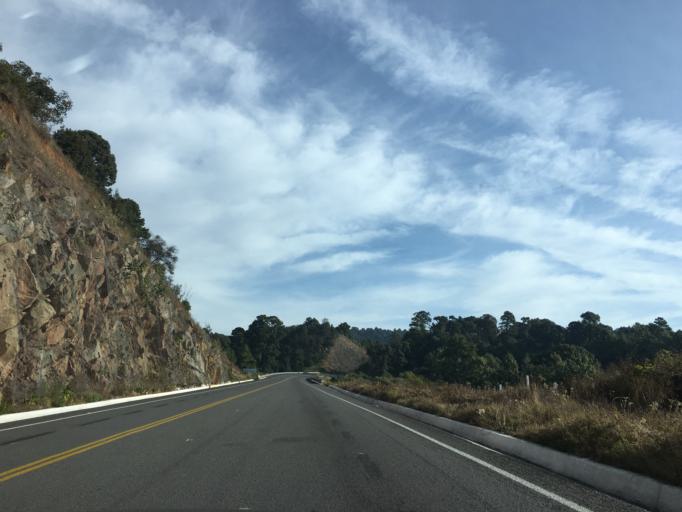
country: MX
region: Mexico
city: San Bartolo
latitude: 19.2677
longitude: -100.0625
